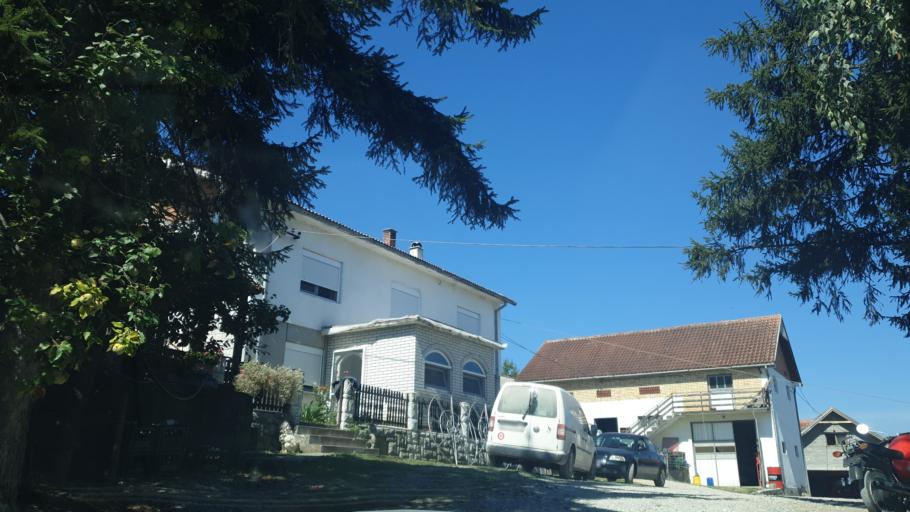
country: RS
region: Central Serbia
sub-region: Kolubarski Okrug
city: Mionica
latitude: 44.1985
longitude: 20.0220
